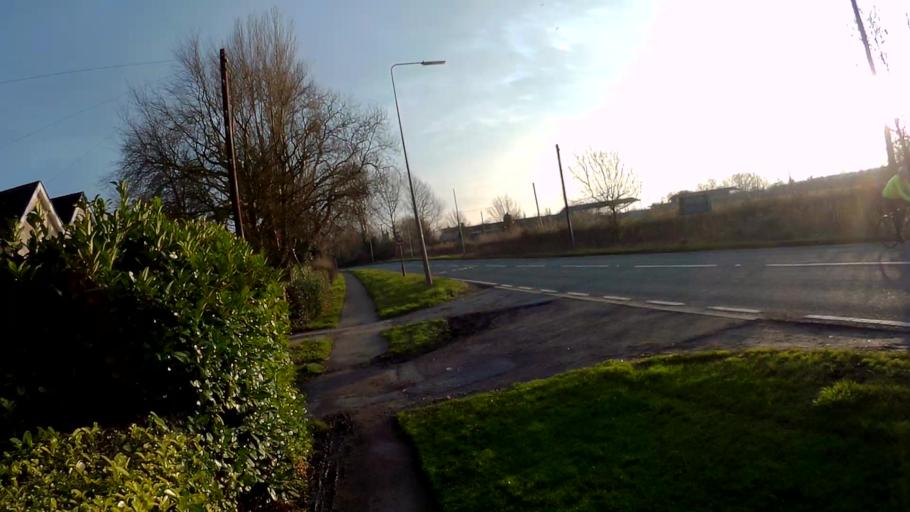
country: GB
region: England
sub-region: Lincolnshire
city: Bourne
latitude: 52.8001
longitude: -0.3790
